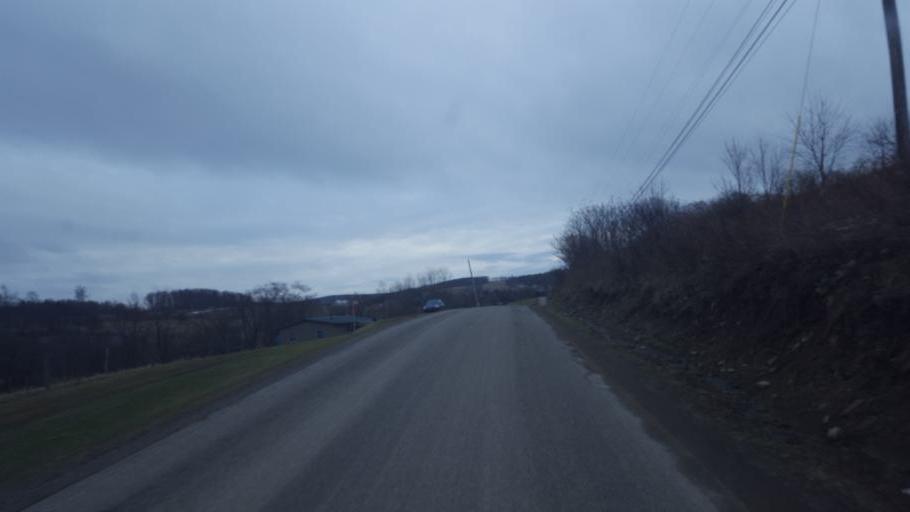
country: US
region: Pennsylvania
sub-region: Potter County
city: Galeton
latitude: 41.9152
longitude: -77.7768
